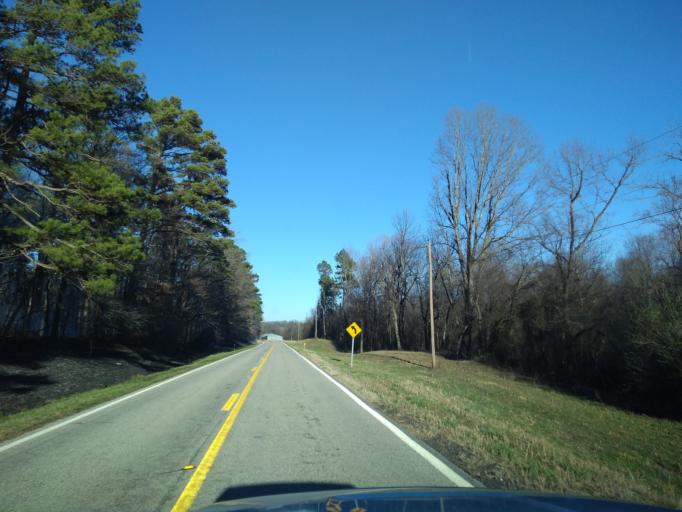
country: US
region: Arkansas
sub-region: Washington County
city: Farmington
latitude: 36.0944
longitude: -94.3582
